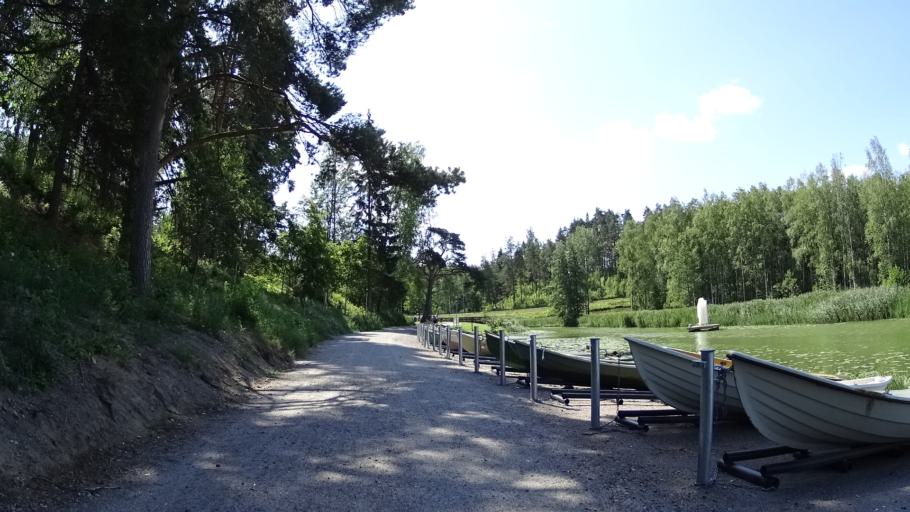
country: FI
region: Uusimaa
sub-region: Helsinki
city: Tuusula
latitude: 60.4054
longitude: 25.0221
